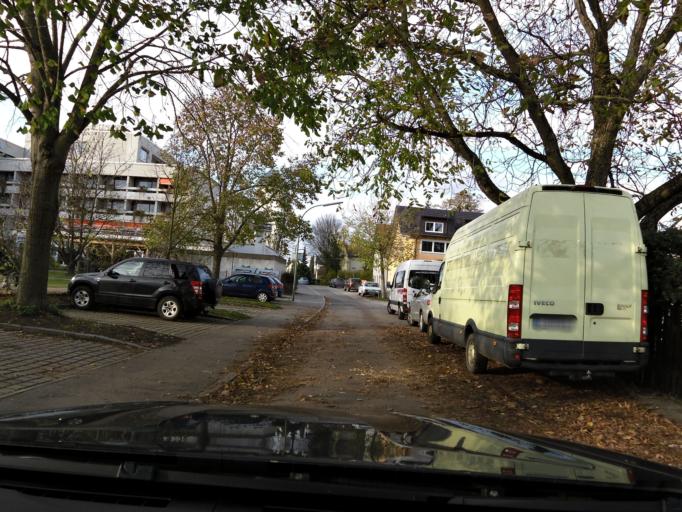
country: DE
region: Bavaria
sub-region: Lower Bavaria
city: Landshut
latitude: 48.5273
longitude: 12.1636
